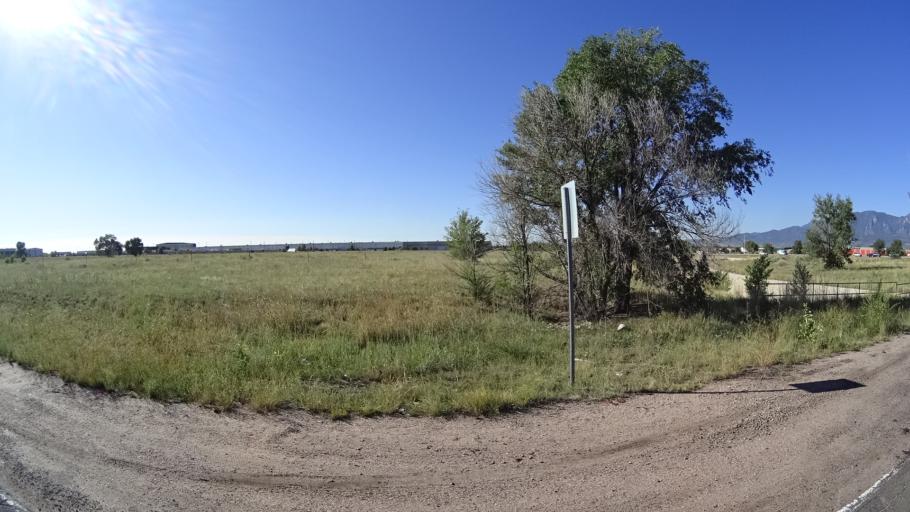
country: US
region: Colorado
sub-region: El Paso County
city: Cimarron Hills
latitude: 38.8061
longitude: -104.7282
